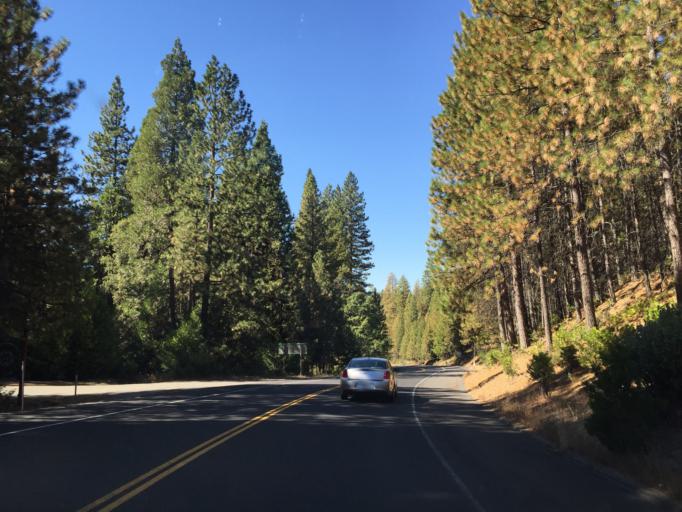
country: US
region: California
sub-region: Tuolumne County
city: Twain Harte
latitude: 38.0441
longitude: -120.2111
